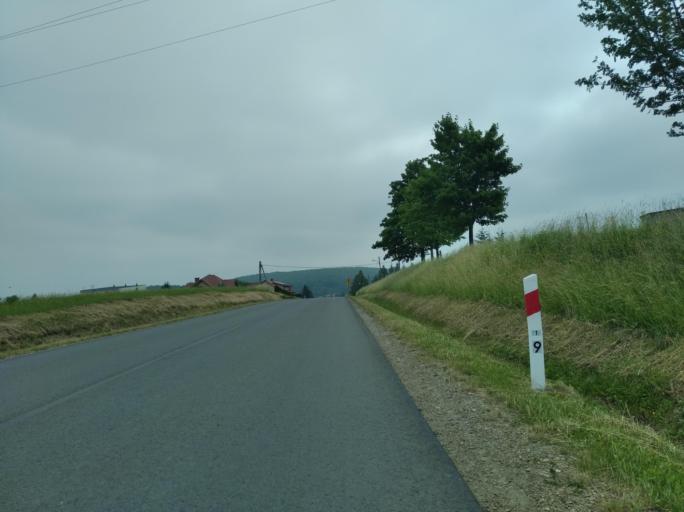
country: PL
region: Subcarpathian Voivodeship
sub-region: Powiat krosnienski
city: Sieniawa
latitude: 49.5648
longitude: 21.9250
